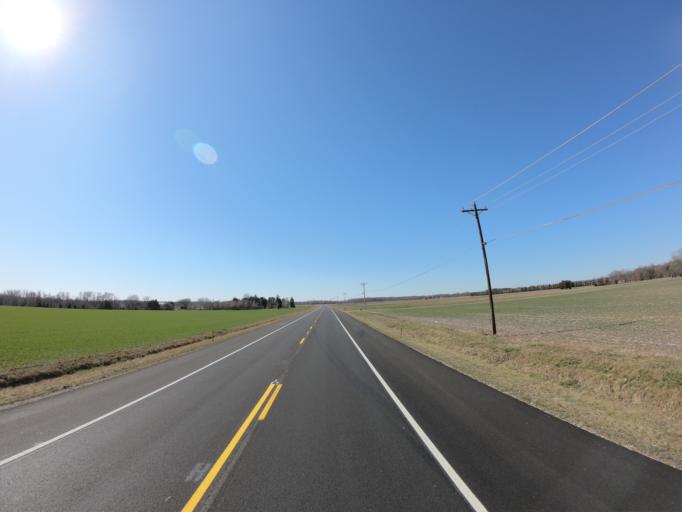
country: US
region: Delaware
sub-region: New Castle County
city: Townsend
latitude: 39.3614
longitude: -75.8261
